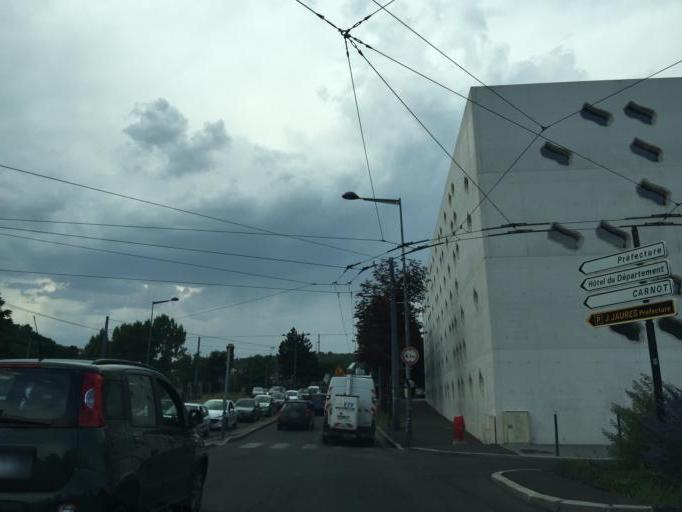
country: FR
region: Rhone-Alpes
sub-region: Departement de la Loire
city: Saint-Etienne
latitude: 45.4372
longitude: 4.3790
